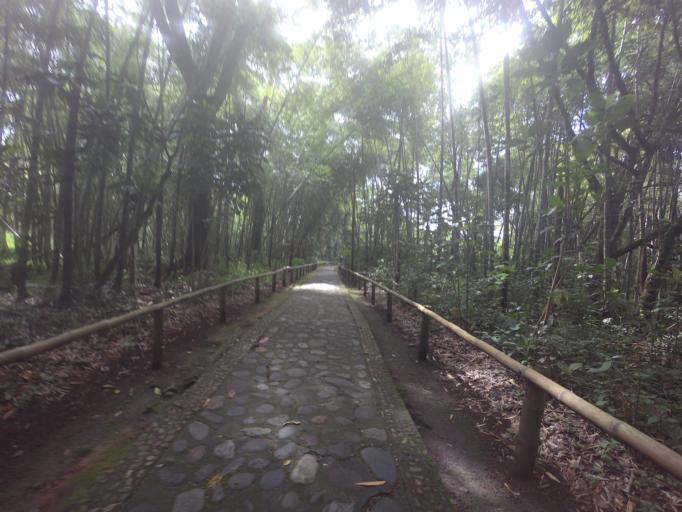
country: CO
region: Huila
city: San Agustin
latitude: 1.8847
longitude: -76.2944
